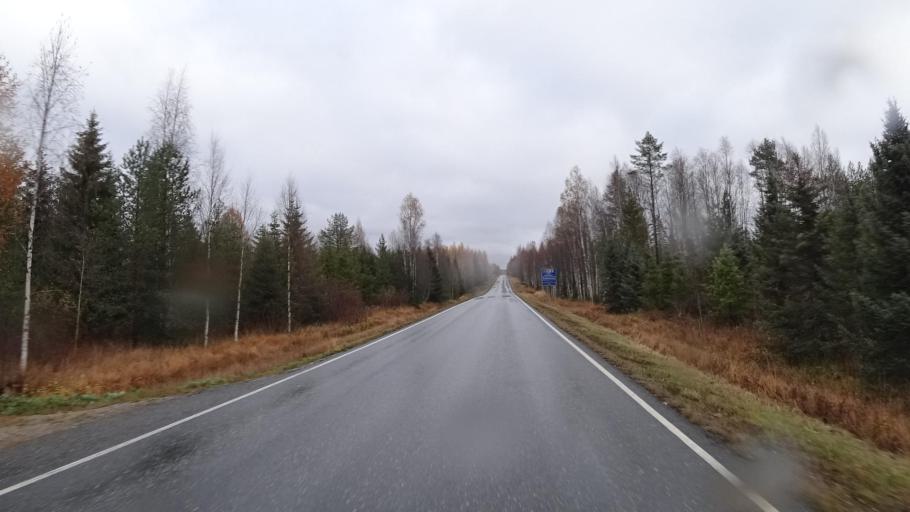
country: FI
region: North Karelia
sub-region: Joensuu
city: Polvijaervi
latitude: 63.0886
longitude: 29.5946
